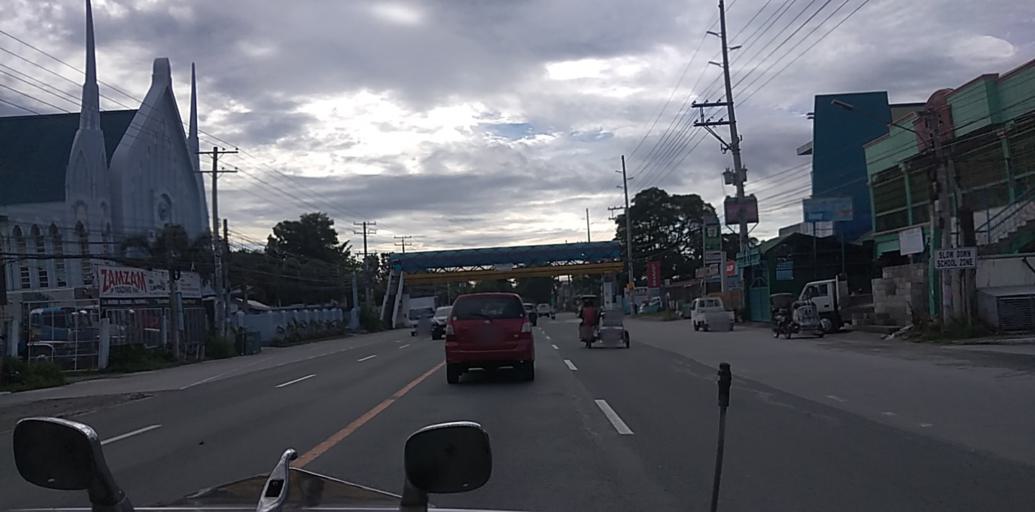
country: PH
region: Central Luzon
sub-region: Province of Pampanga
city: Telabastagan
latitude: 15.0937
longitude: 120.6267
